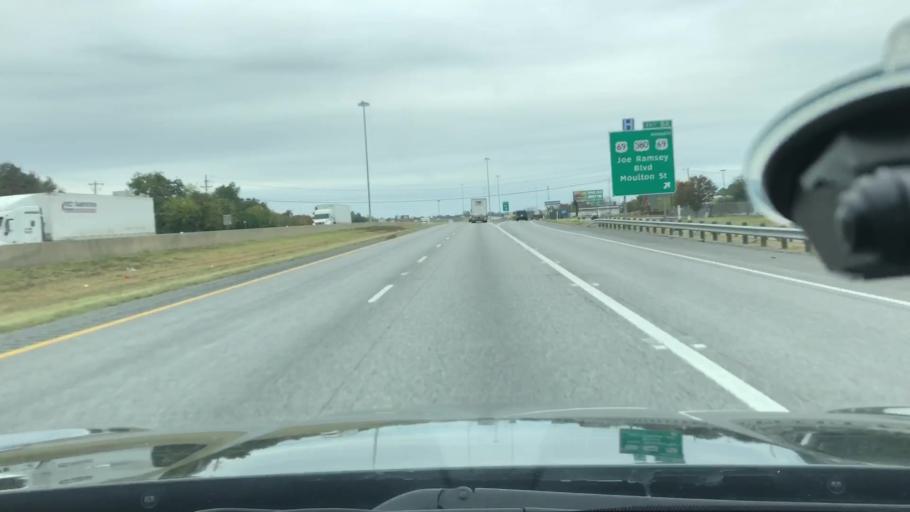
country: US
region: Texas
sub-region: Hunt County
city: Greenville
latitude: 33.1063
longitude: -96.1028
